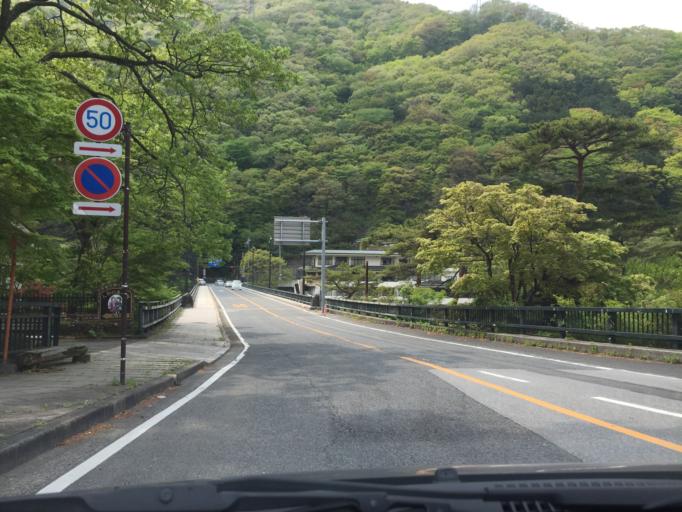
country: JP
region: Tochigi
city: Imaichi
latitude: 36.8424
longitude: 139.7225
